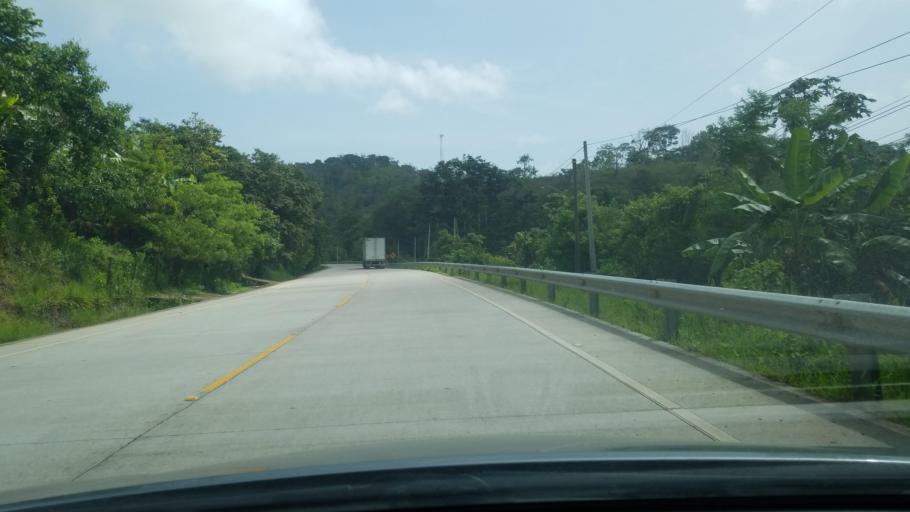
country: HN
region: Copan
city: San Jeronimo
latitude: 14.9430
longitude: -88.9147
